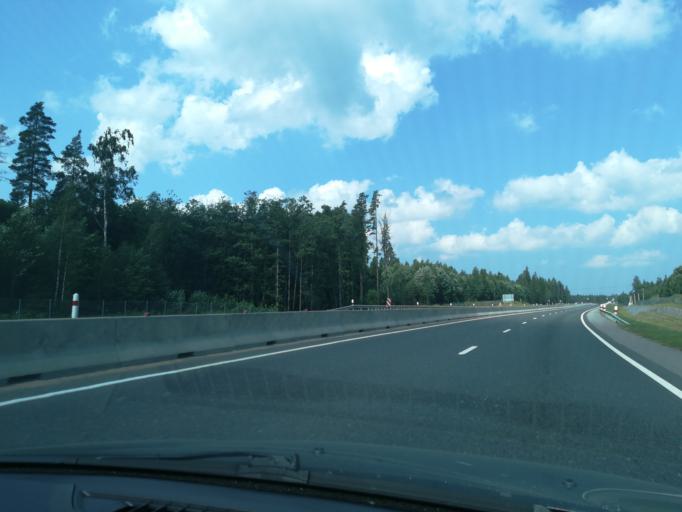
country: RU
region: Leningrad
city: Vistino
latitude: 59.6365
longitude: 28.5733
